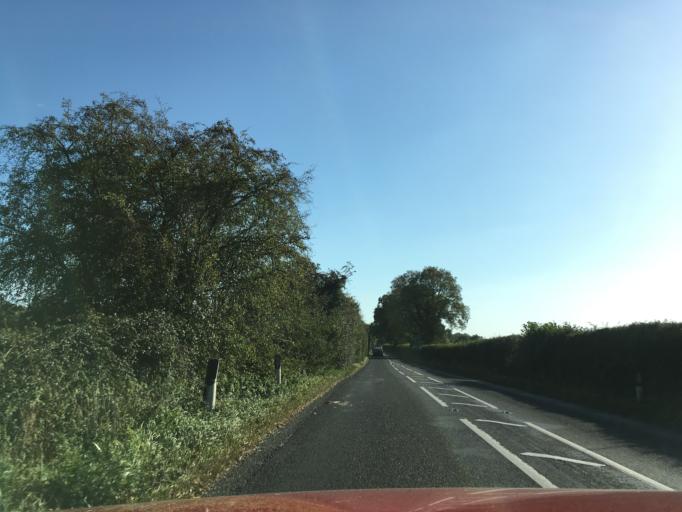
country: GB
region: England
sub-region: Hampshire
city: Swanmore
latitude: 50.9932
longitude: -1.1188
